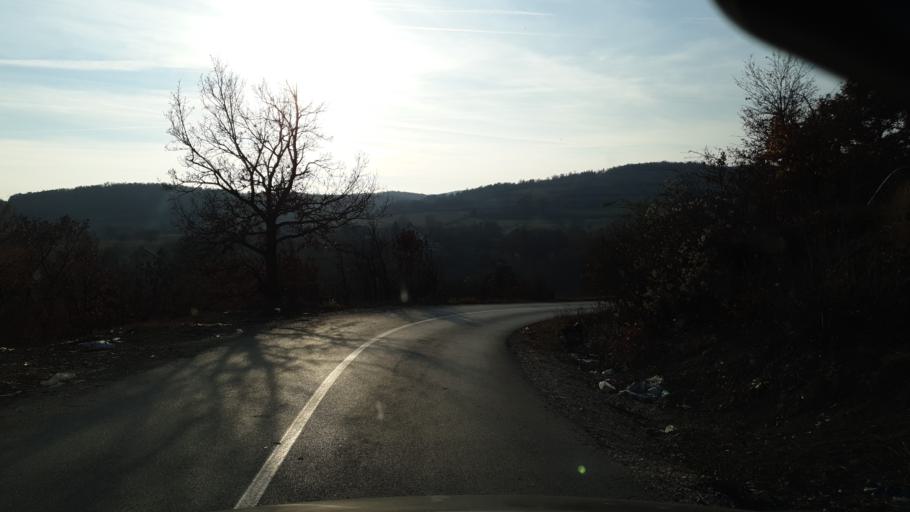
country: RS
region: Central Serbia
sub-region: Borski Okrug
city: Bor
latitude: 44.0472
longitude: 22.0789
